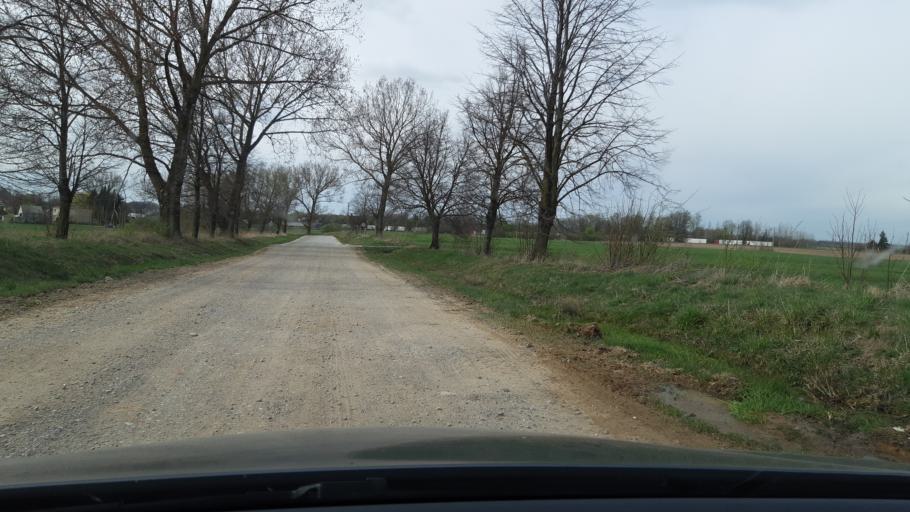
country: LT
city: Virbalis
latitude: 54.6208
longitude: 22.8377
